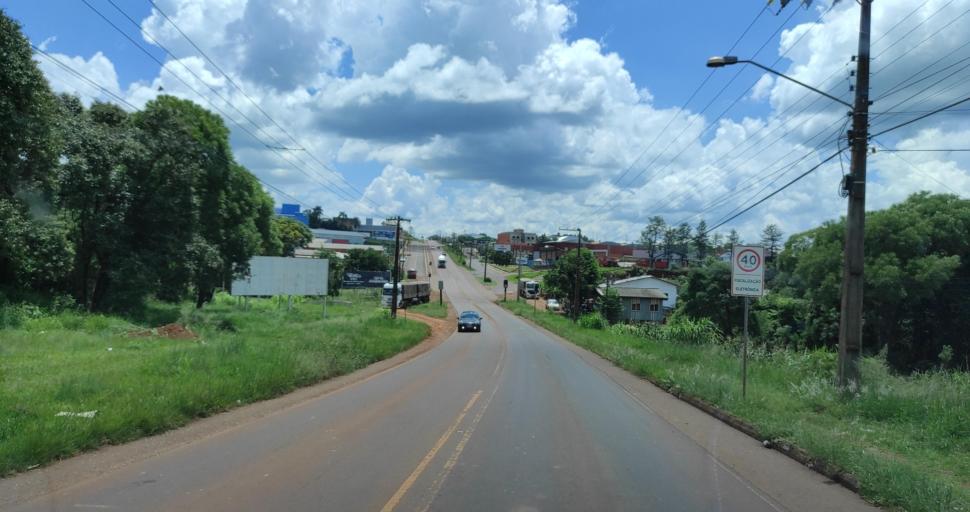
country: BR
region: Santa Catarina
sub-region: Xanxere
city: Xanxere
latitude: -26.8620
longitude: -52.4067
